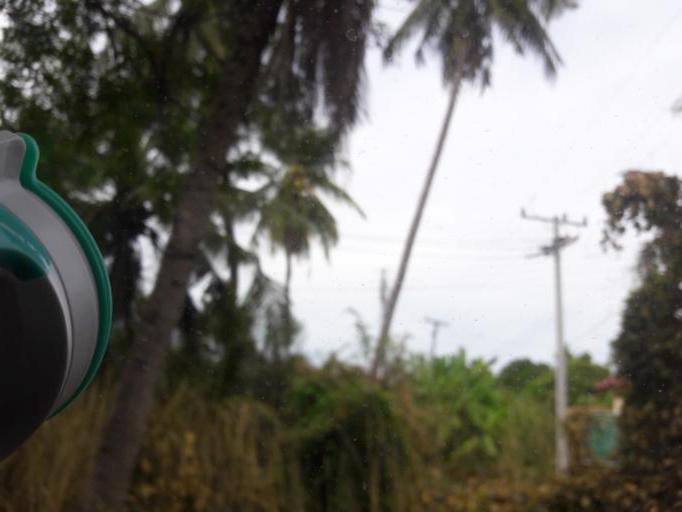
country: TH
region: Ratchaburi
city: Damnoen Saduak
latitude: 13.5198
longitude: 100.0058
